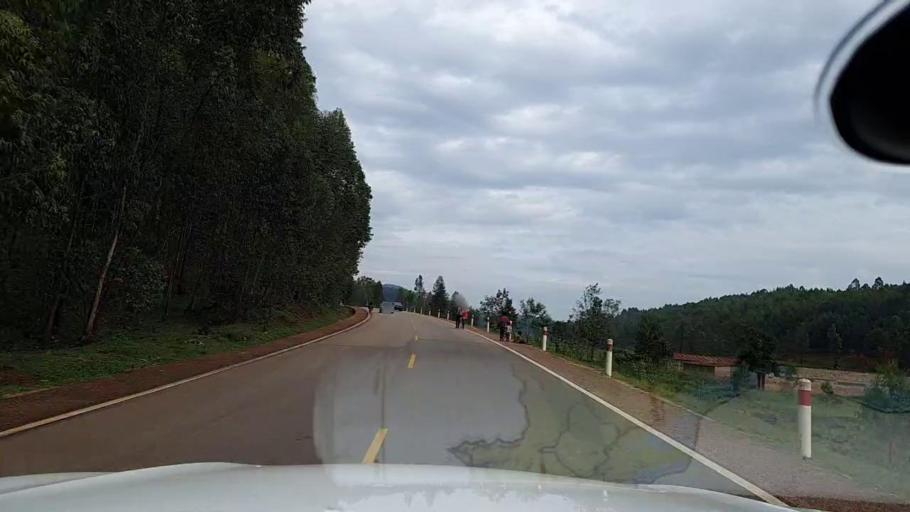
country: RW
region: Southern Province
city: Butare
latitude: -2.5631
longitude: 29.7227
